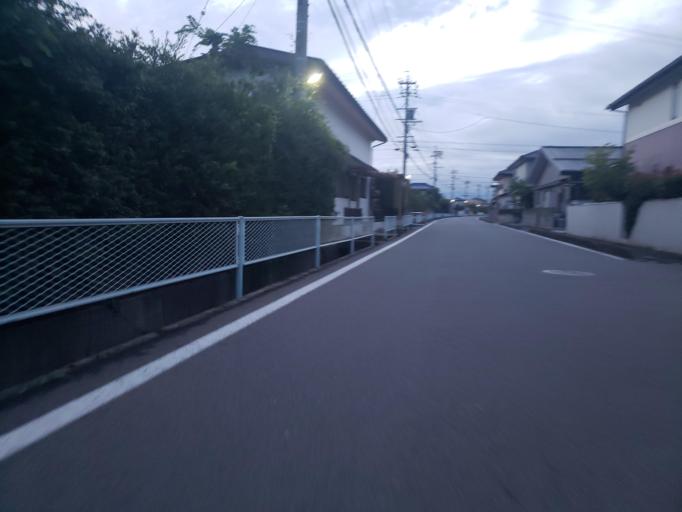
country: JP
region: Nagano
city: Nagano-shi
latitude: 36.6303
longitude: 138.1685
